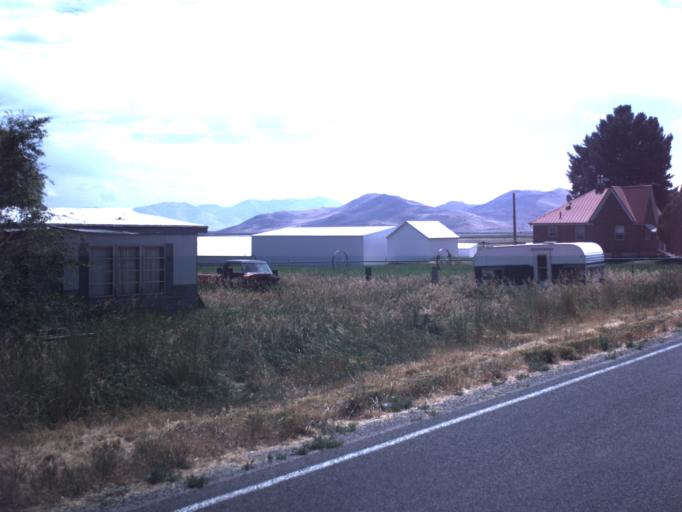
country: US
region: Utah
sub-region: Box Elder County
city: Tremonton
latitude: 41.6710
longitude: -112.2966
